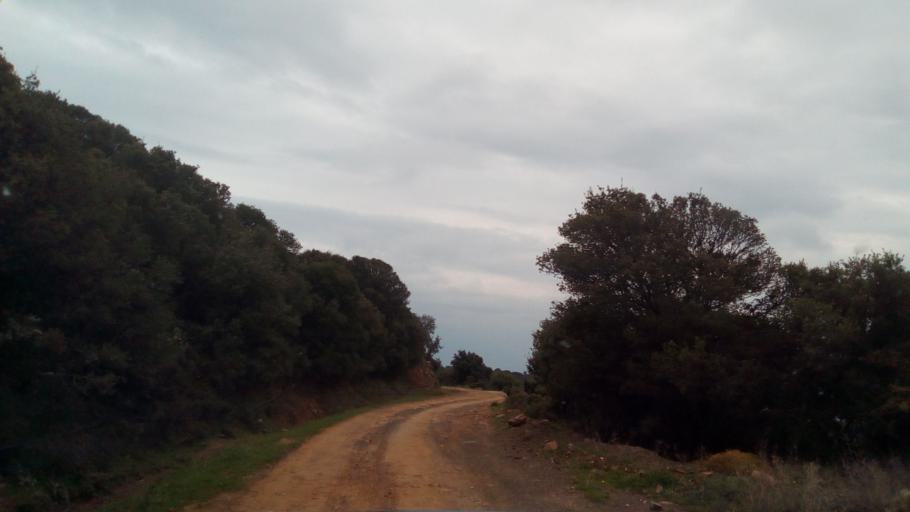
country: GR
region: West Greece
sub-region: Nomos Achaias
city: Selianitika
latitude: 38.4052
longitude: 22.0869
